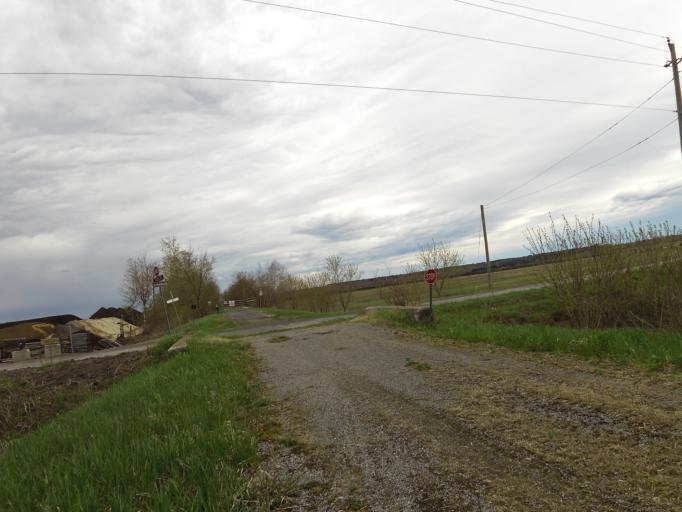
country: CA
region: Quebec
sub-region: Outaouais
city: Papineauville
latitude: 45.5404
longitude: -74.8571
